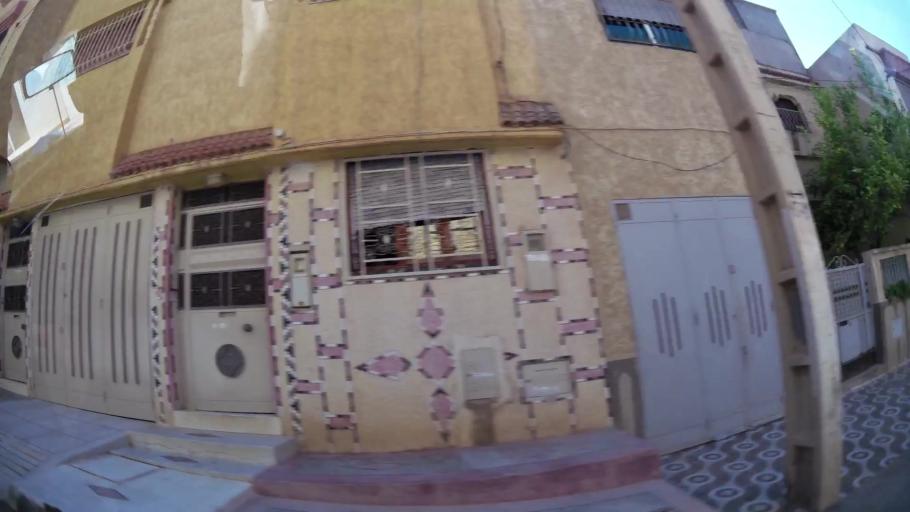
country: MA
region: Oriental
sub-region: Oujda-Angad
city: Oujda
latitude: 34.6899
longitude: -1.8714
